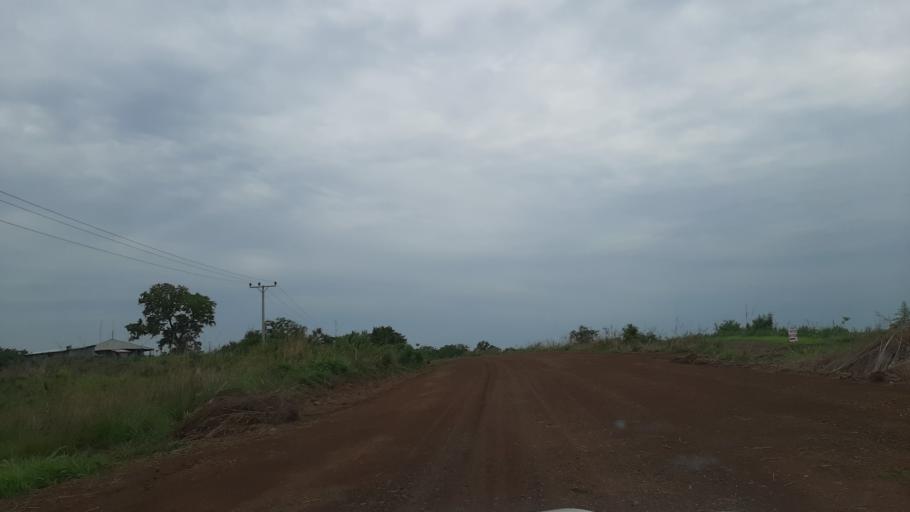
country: ET
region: Gambela
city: Gambela
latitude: 8.2180
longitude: 34.5247
